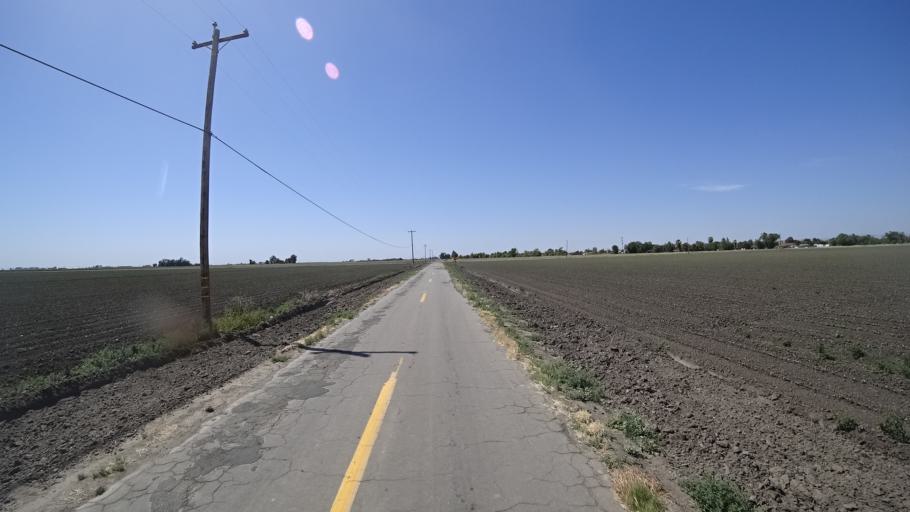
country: US
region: California
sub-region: Kings County
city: Stratford
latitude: 36.1988
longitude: -119.8162
